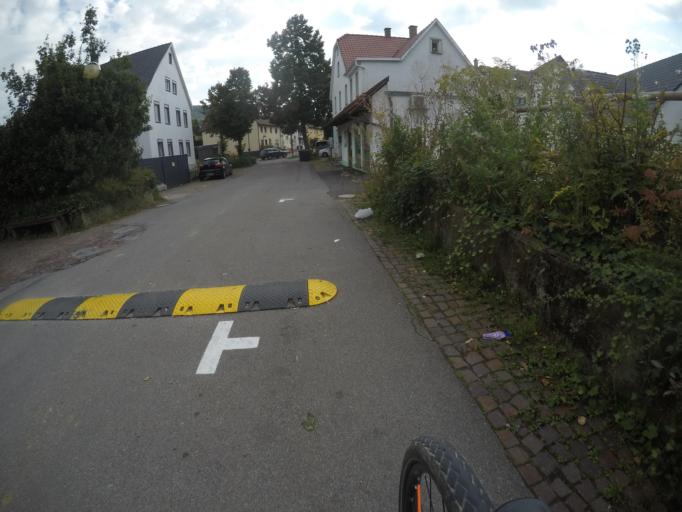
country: DE
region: Baden-Wuerttemberg
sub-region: Tuebingen Region
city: Dettingen an der Erms
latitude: 48.5299
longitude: 9.3495
